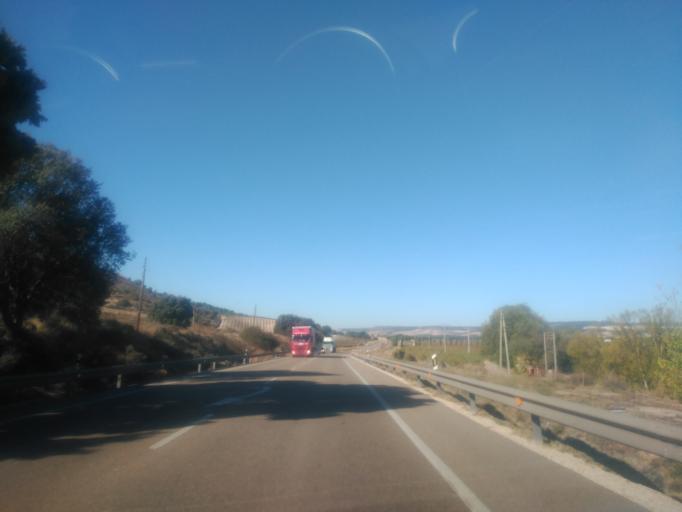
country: ES
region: Castille and Leon
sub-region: Provincia de Valladolid
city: Valbuena de Duero
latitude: 41.6251
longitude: -4.2744
